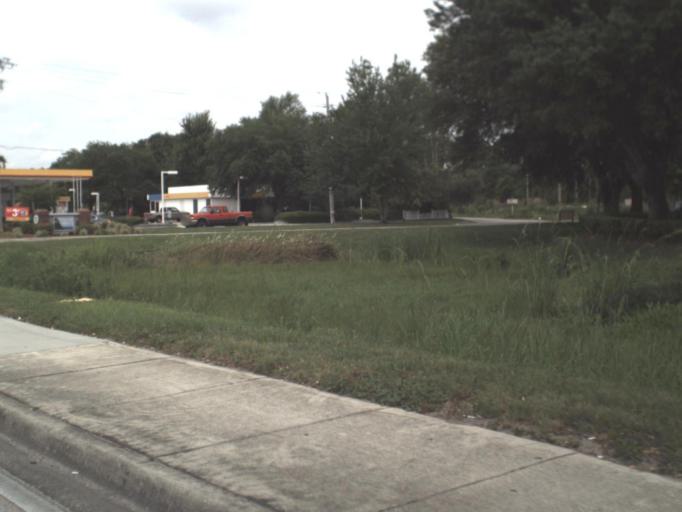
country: US
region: Florida
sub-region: Clay County
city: Lakeside
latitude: 30.1422
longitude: -81.7670
